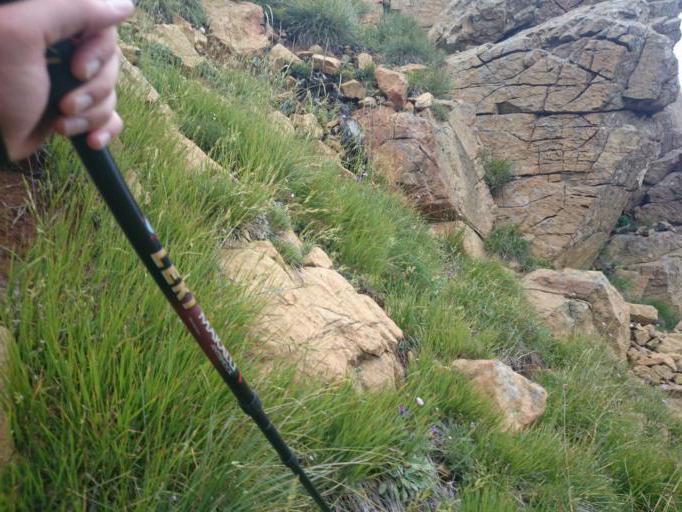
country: AL
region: Diber
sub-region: Rrethi i Dibres
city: Fushe-Lure
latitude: 41.7845
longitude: 20.1831
